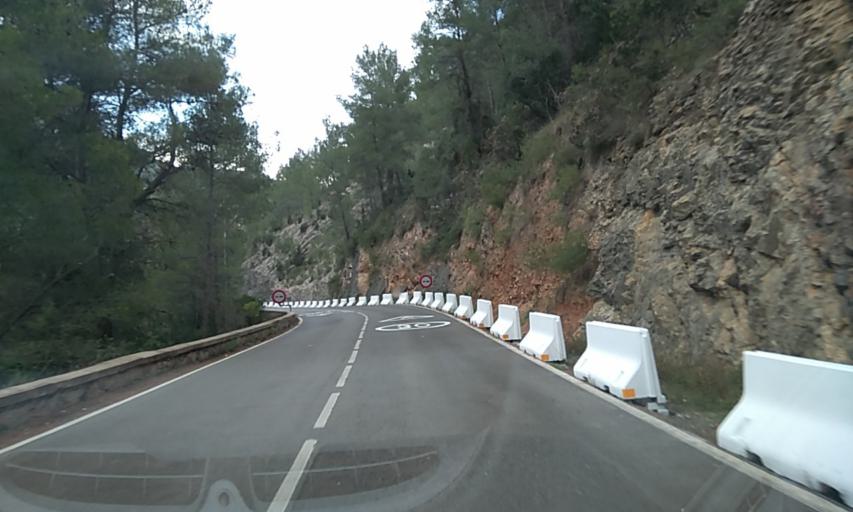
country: ES
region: Valencia
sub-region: Provincia de Castello
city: Montanejos
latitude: 40.0736
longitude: -0.5341
